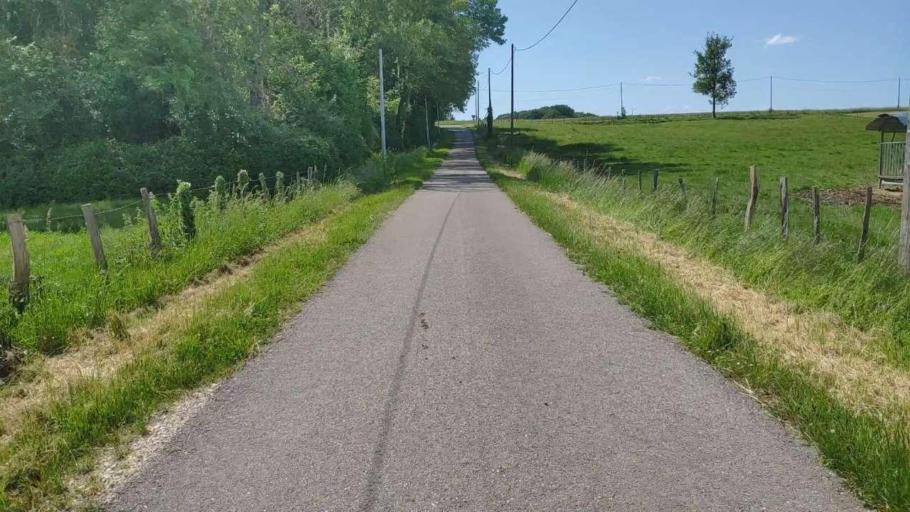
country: FR
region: Franche-Comte
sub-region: Departement du Jura
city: Bletterans
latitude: 46.8050
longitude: 5.4125
